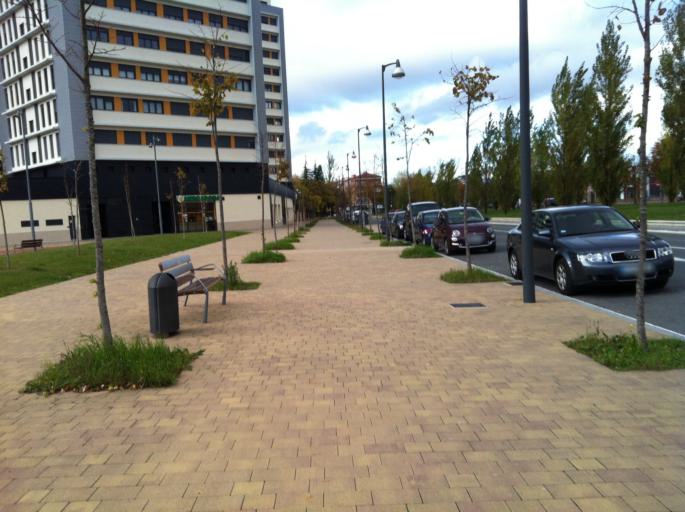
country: ES
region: Basque Country
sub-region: Provincia de Alava
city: Gasteiz / Vitoria
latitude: 42.8338
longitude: -2.6580
